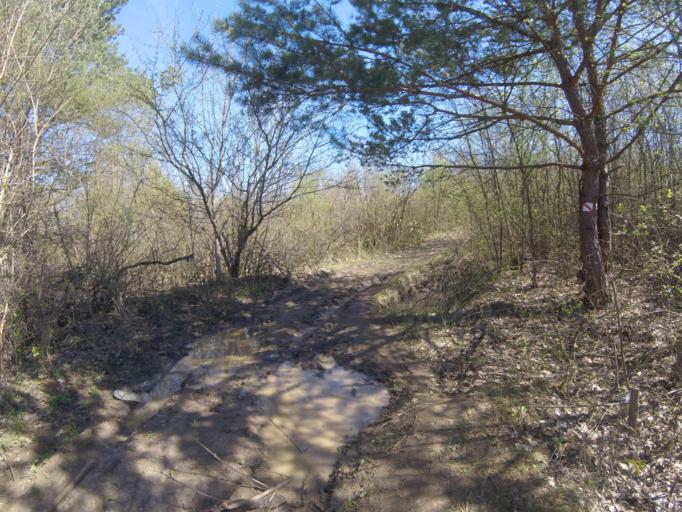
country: HU
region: Borsod-Abauj-Zemplen
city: Szendro
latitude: 48.4065
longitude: 20.7572
